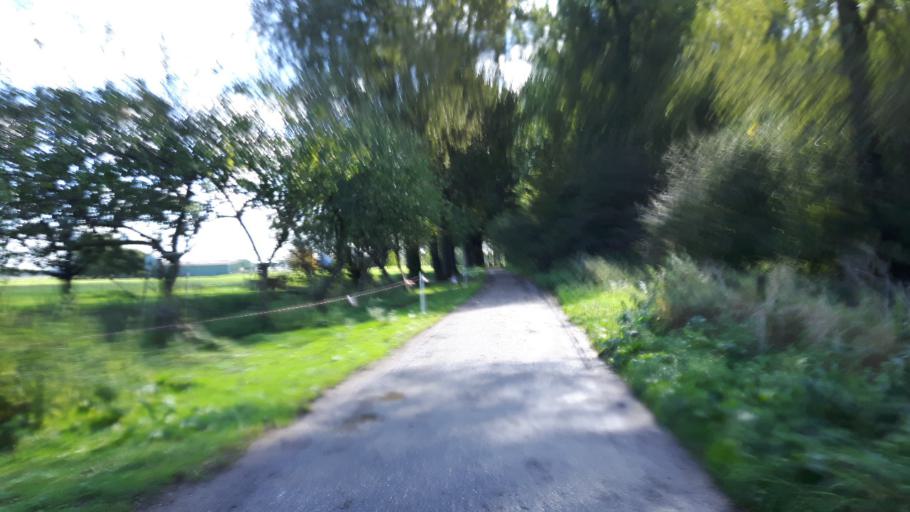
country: NL
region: Gelderland
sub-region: Gemeente Culemborg
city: Culemborg
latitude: 51.9394
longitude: 5.2522
